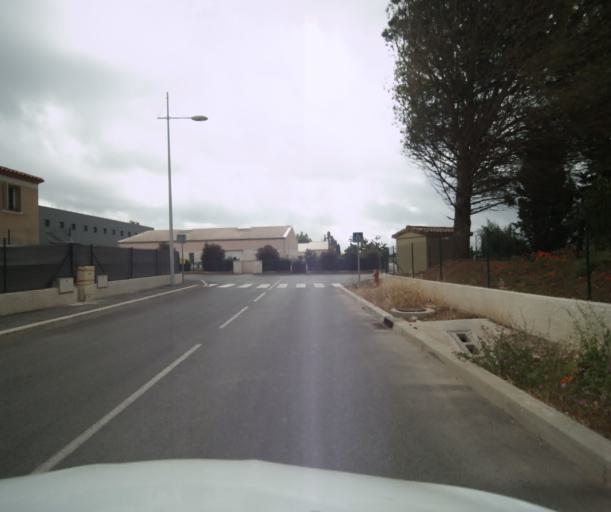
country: FR
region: Provence-Alpes-Cote d'Azur
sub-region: Departement du Var
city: Ollioules
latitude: 43.1267
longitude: 5.8588
